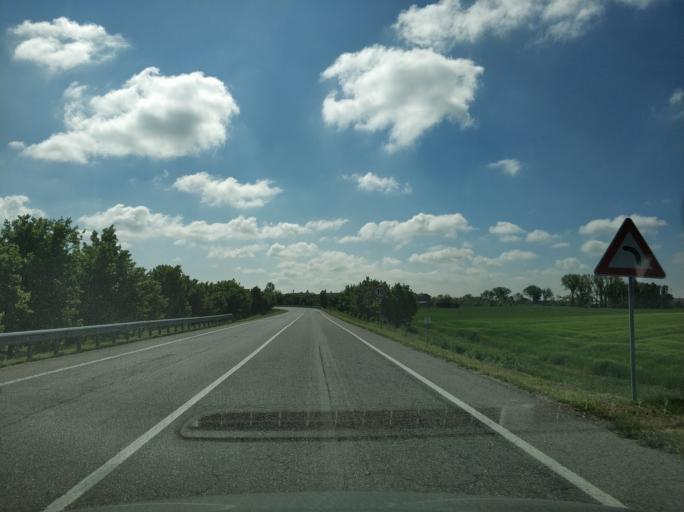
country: IT
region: Veneto
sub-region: Provincia di Venezia
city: Arino
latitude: 45.4341
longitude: 12.0423
